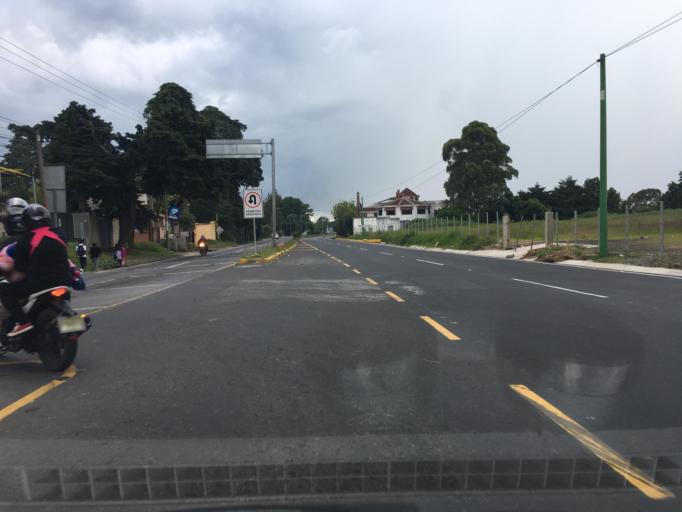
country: GT
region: Guatemala
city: Fraijanes
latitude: 14.4675
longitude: -90.4844
